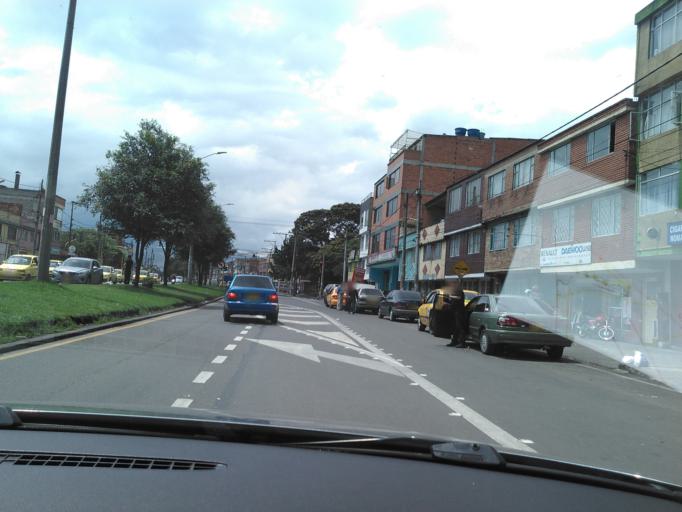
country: CO
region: Bogota D.C.
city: Bogota
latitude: 4.6199
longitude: -74.1123
